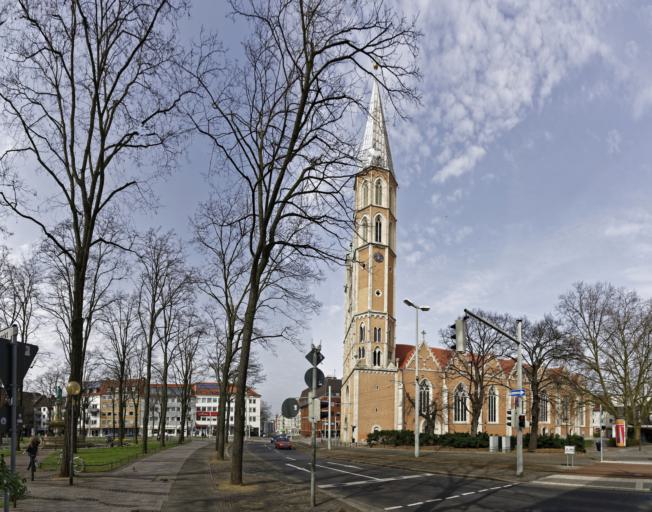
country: DE
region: Lower Saxony
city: Braunschweig
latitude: 52.2669
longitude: 10.5250
